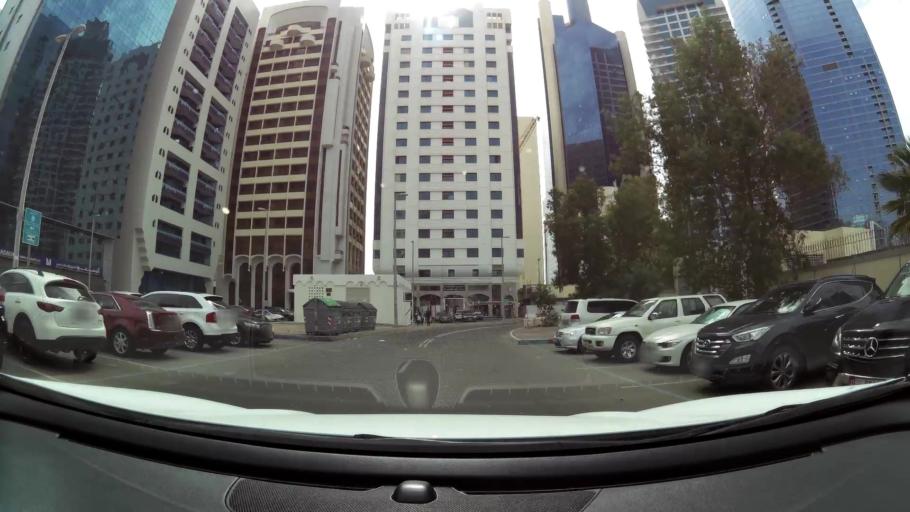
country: AE
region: Abu Dhabi
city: Abu Dhabi
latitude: 24.4827
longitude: 54.3517
